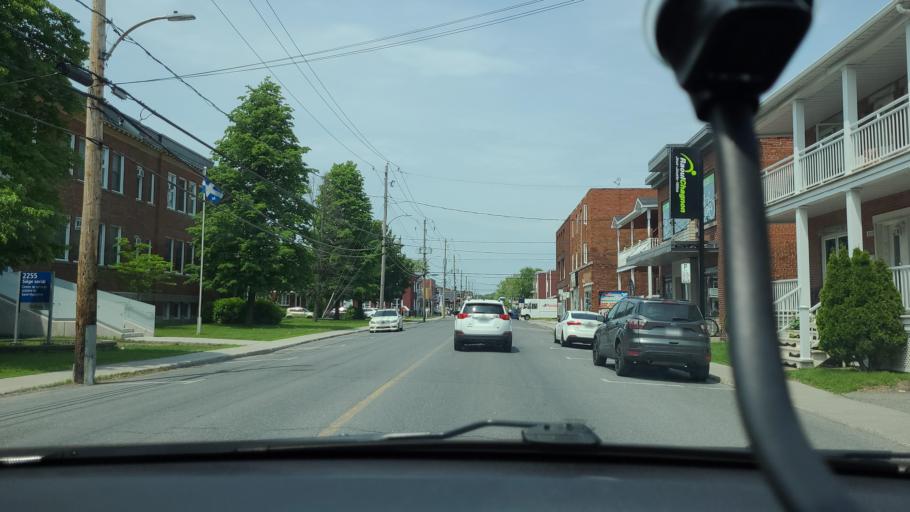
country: CA
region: Quebec
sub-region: Monteregie
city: Saint-Hyacinthe
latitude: 45.6293
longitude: -72.9538
